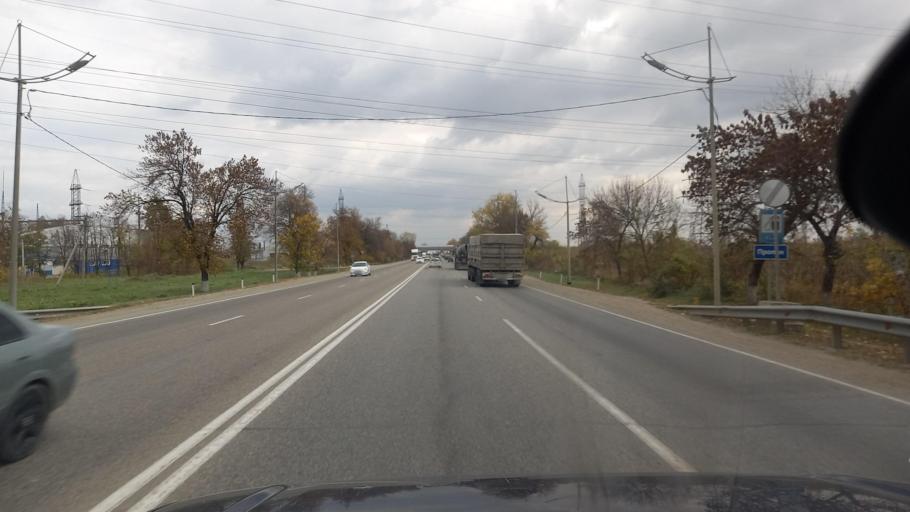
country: RU
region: Krasnodarskiy
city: Afipskiy
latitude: 44.8865
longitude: 38.8452
